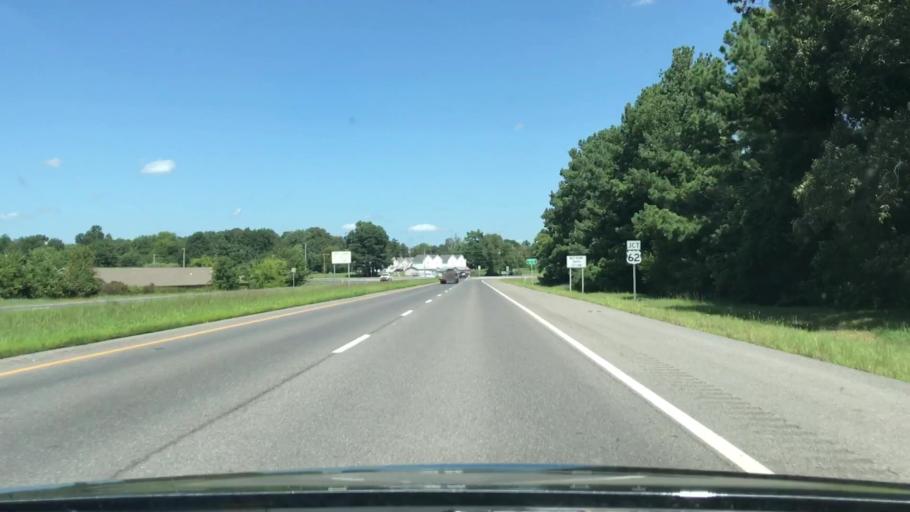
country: US
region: Kentucky
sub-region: McCracken County
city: Reidland
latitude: 37.0071
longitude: -88.5077
